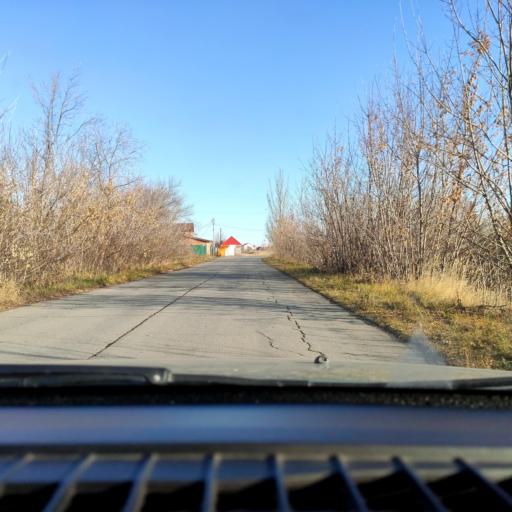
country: RU
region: Samara
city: Tol'yatti
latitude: 53.6634
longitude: 49.3361
